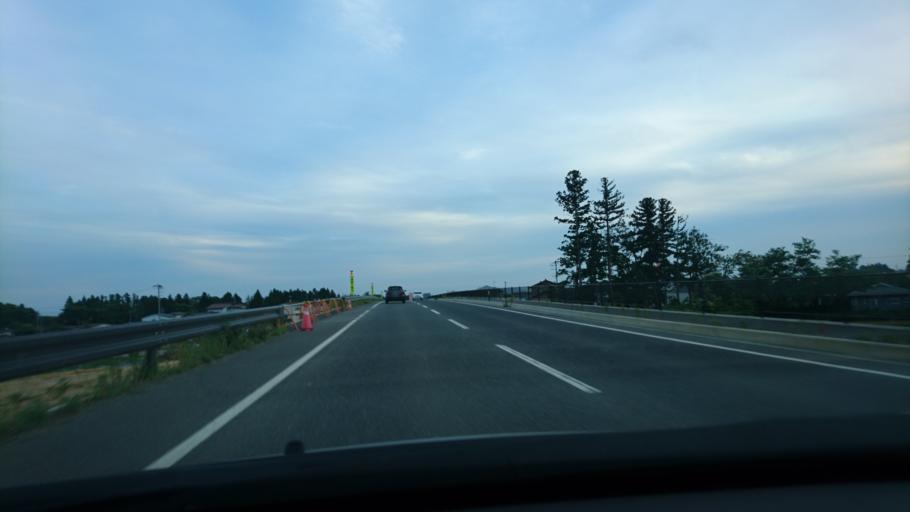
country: JP
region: Miyagi
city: Furukawa
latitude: 38.7388
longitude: 141.0381
